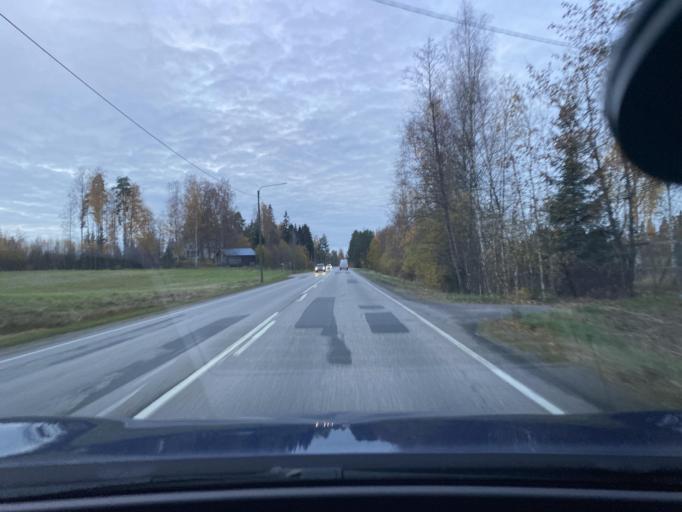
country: FI
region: Uusimaa
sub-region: Helsinki
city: Vihti
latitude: 60.3366
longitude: 24.1990
